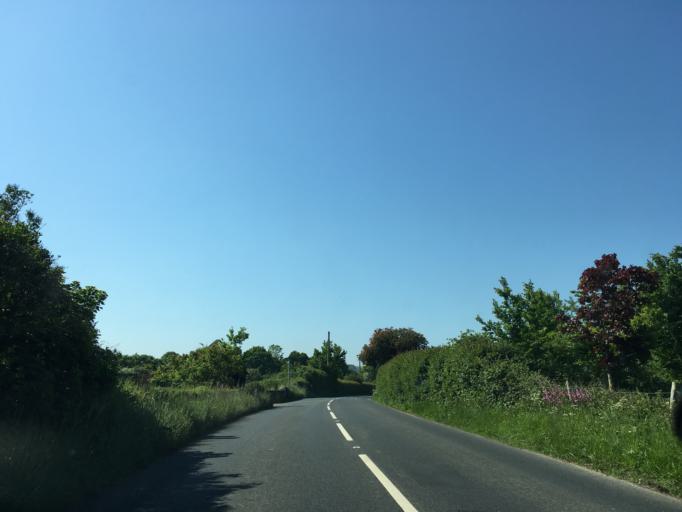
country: GB
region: England
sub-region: Isle of Wight
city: Ryde
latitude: 50.7041
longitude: -1.1669
